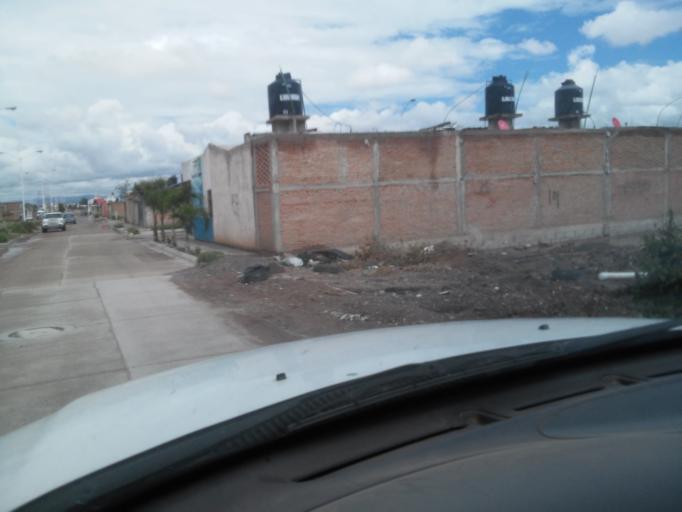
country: MX
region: Durango
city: Victoria de Durango
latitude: 24.0213
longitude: -104.6128
